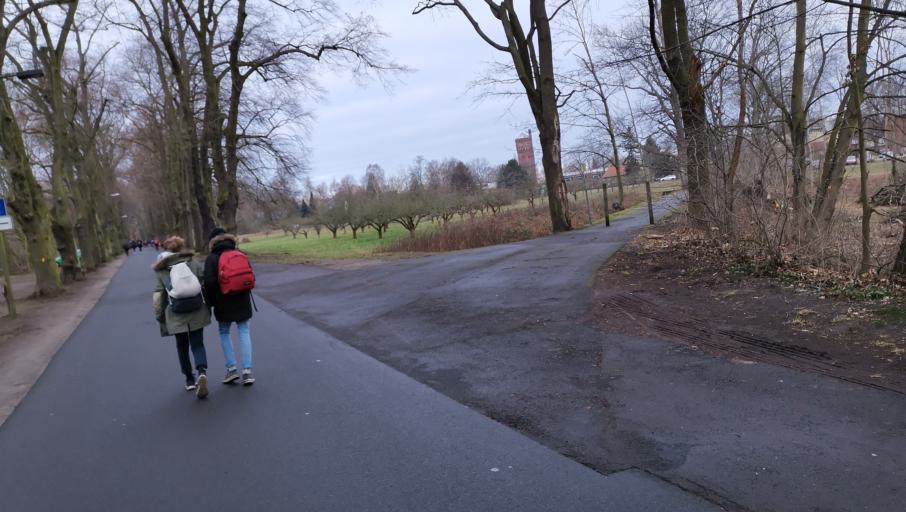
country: DE
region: Brandenburg
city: Potsdam
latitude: 52.3835
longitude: 13.0406
